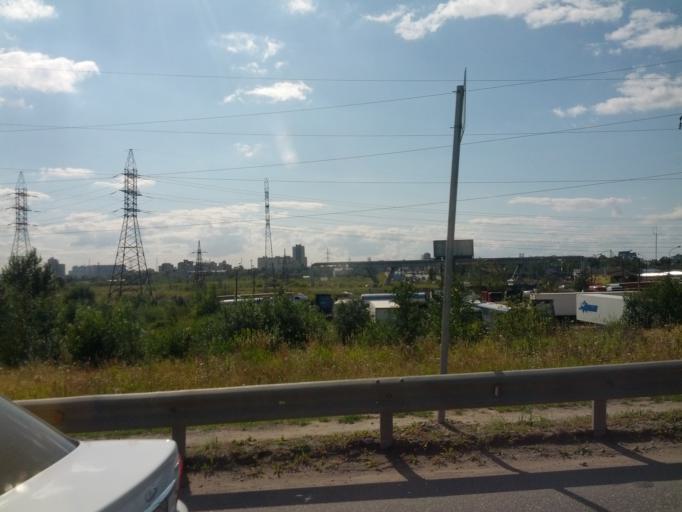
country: RU
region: Leningrad
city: Rybatskoye
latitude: 59.8865
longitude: 30.5063
